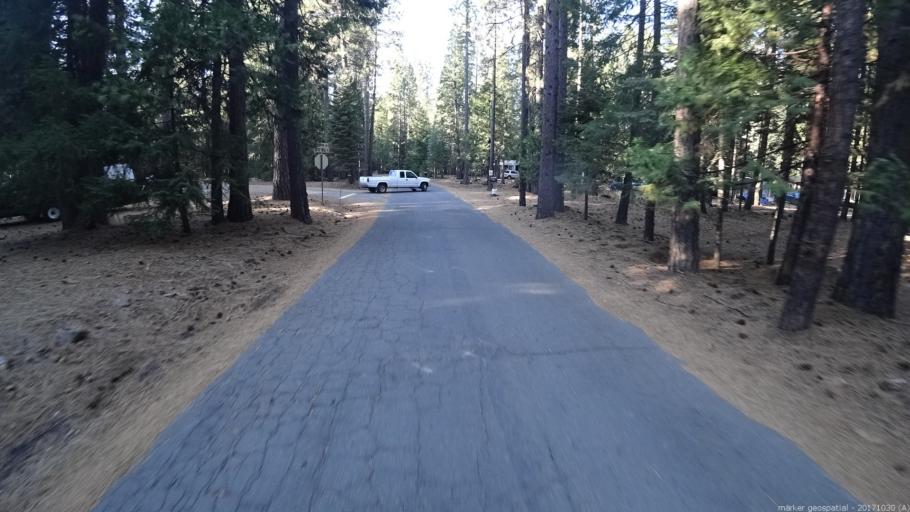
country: US
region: California
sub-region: Shasta County
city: Shingletown
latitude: 40.5521
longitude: -121.7327
